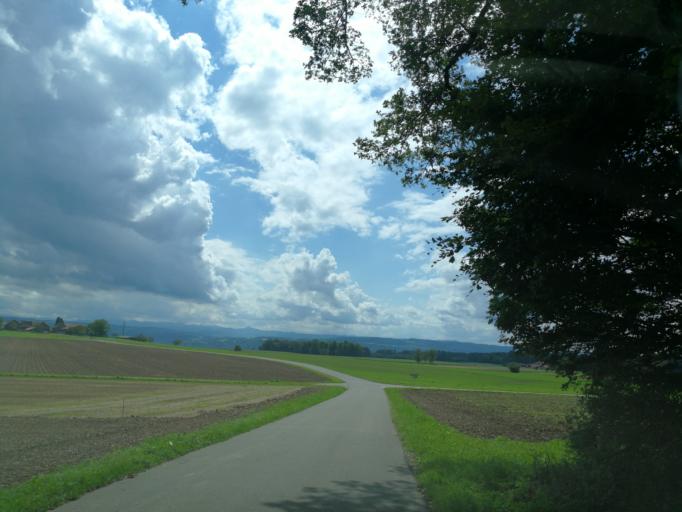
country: CH
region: Thurgau
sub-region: Kreuzlingen District
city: Ermatingen
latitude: 47.6414
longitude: 9.0761
